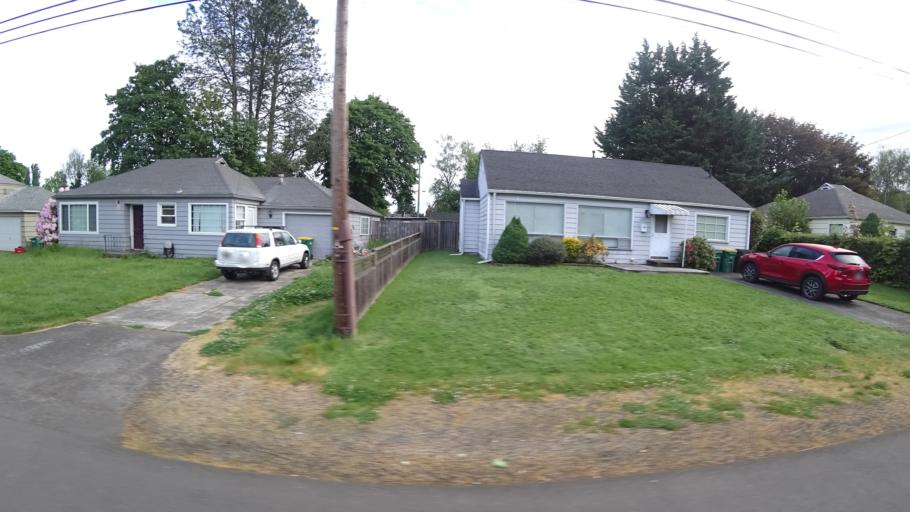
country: US
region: Oregon
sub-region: Washington County
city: Beaverton
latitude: 45.4817
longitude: -122.8135
